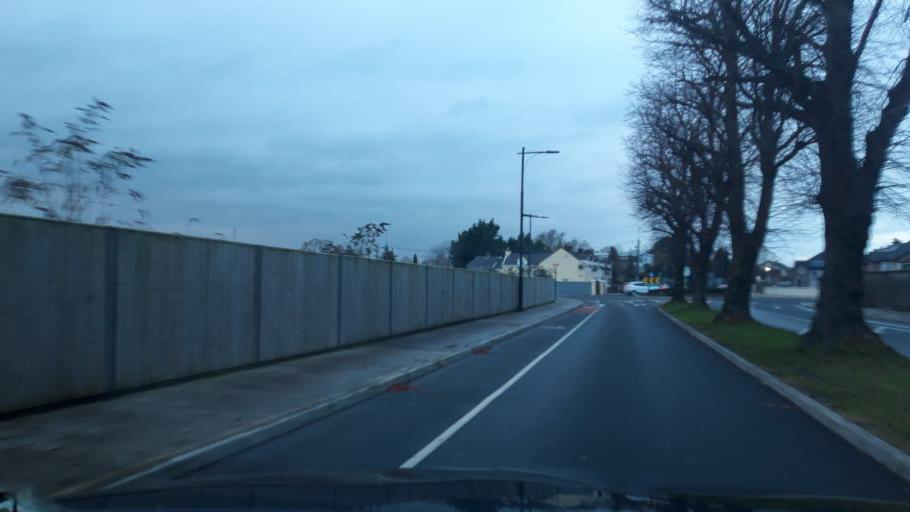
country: IE
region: Leinster
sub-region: Kilkenny
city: Kilkenny
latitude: 52.6590
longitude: -7.2483
